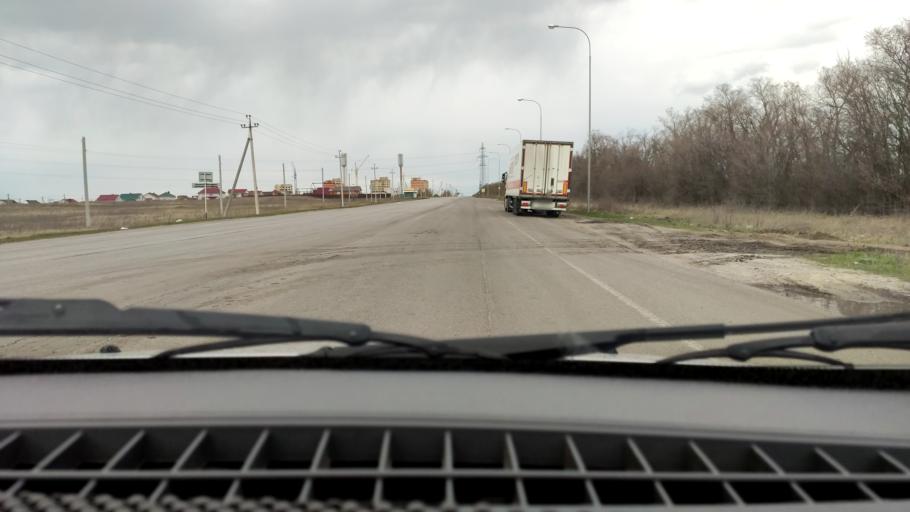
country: RU
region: Voronezj
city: Novaya Usman'
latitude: 51.6210
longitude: 39.3355
